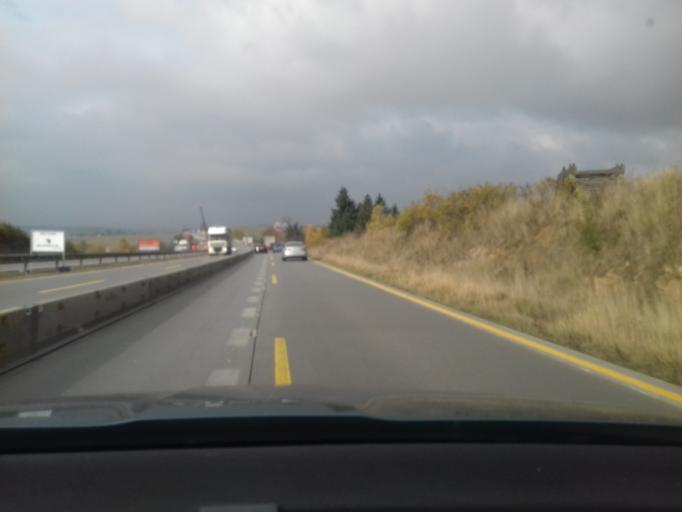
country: CZ
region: Vysocina
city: Merin
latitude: 49.3875
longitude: 15.9190
